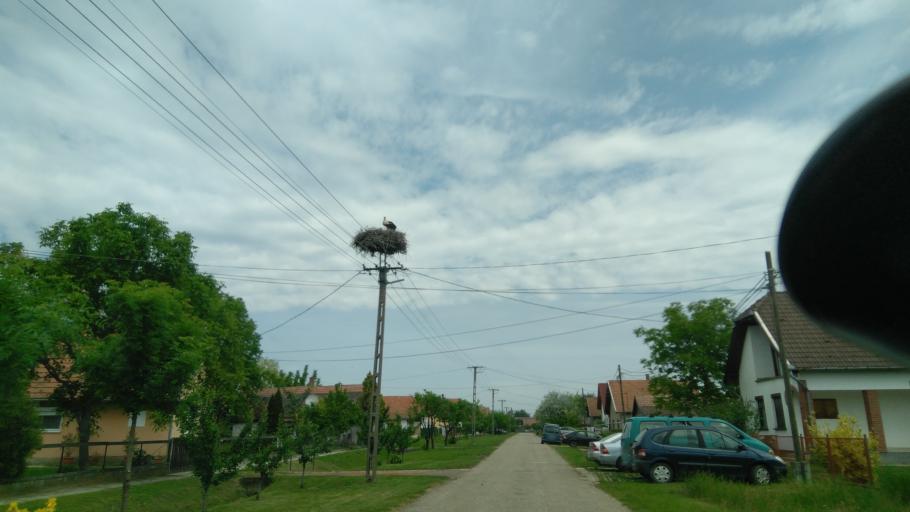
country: HU
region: Bekes
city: Fuzesgyarmat
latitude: 47.0997
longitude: 21.2135
